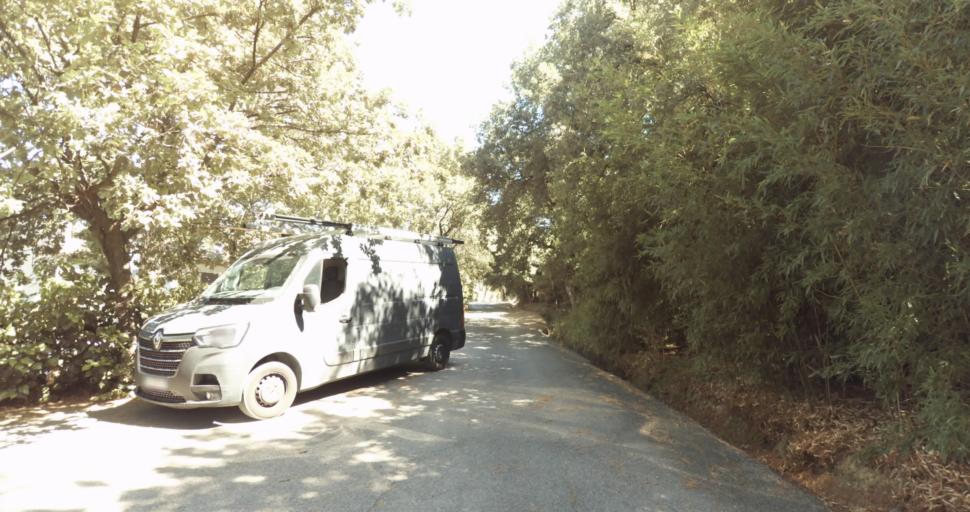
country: FR
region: Provence-Alpes-Cote d'Azur
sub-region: Departement du Var
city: Gassin
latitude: 43.2549
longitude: 6.5996
